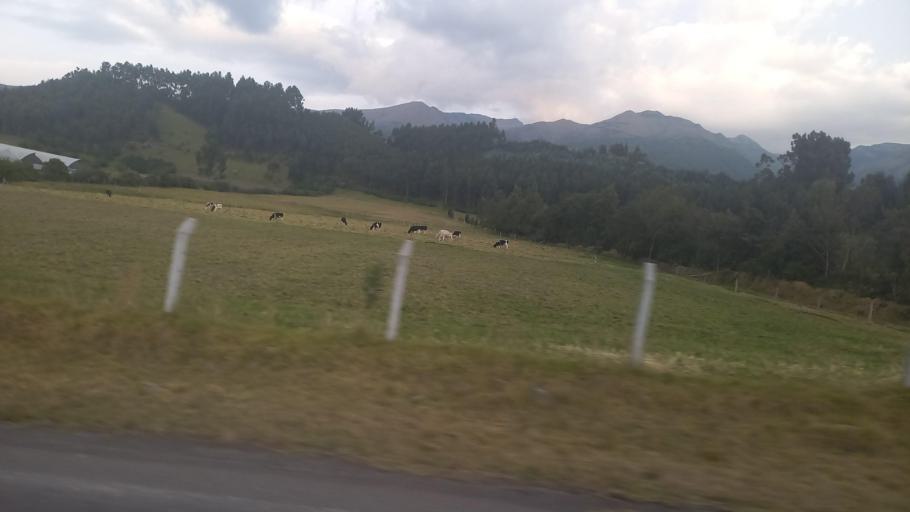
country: EC
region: Pichincha
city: Cayambe
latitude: 0.0769
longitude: -78.1090
